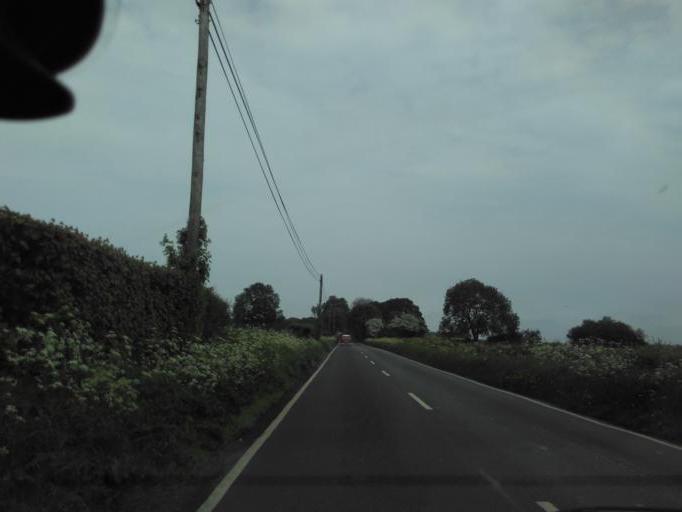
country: GB
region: England
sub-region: Kent
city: Lyminge
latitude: 51.1848
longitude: 1.0543
